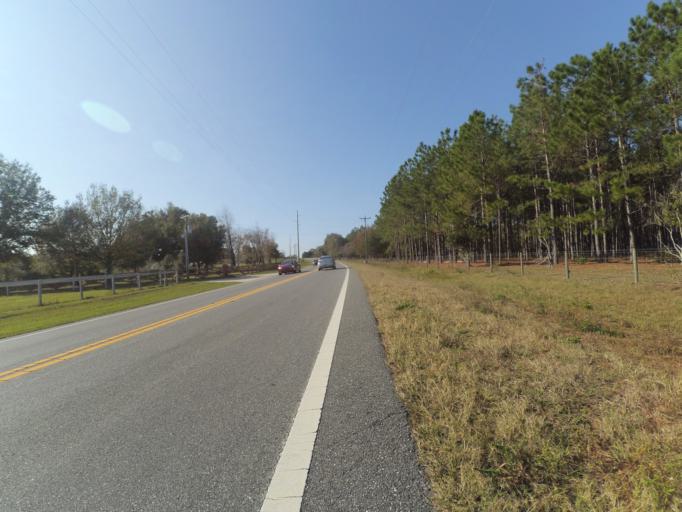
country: US
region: Florida
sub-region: Lake County
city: Umatilla
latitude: 28.9676
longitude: -81.6629
